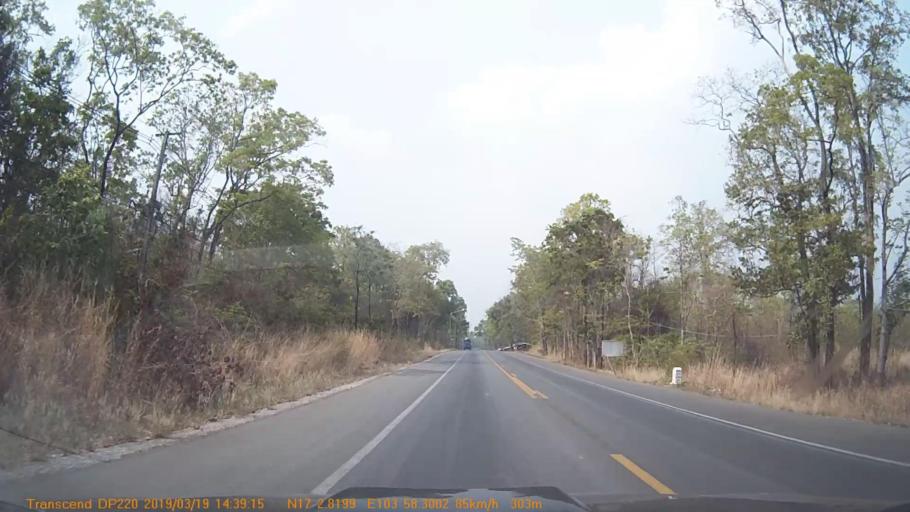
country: TH
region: Sakon Nakhon
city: Phu Phan
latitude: 17.0472
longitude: 103.9717
